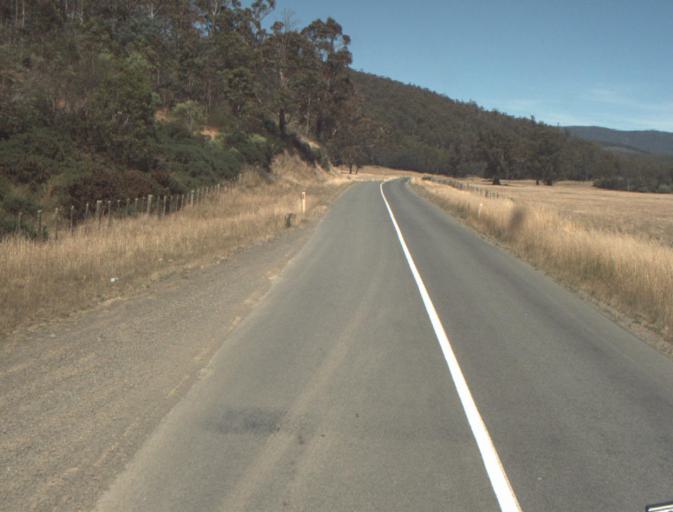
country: AU
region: Tasmania
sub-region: Dorset
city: Scottsdale
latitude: -41.2876
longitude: 147.3843
